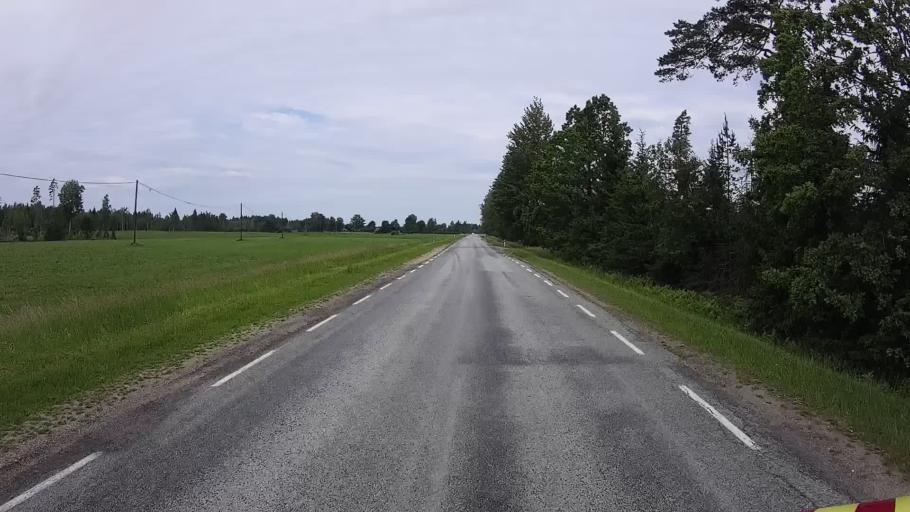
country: EE
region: Viljandimaa
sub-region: Karksi vald
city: Karksi-Nuia
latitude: 58.2240
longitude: 25.6135
